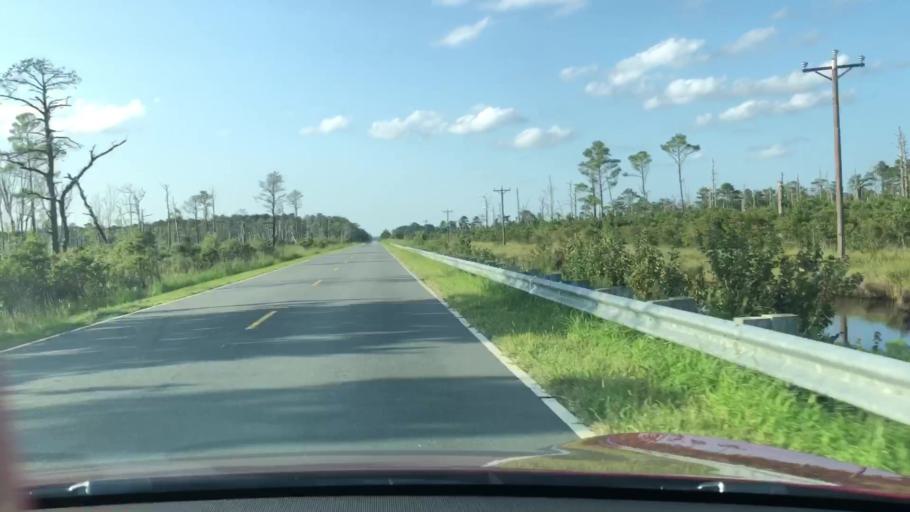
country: US
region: North Carolina
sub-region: Dare County
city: Wanchese
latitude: 35.6625
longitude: -75.7776
